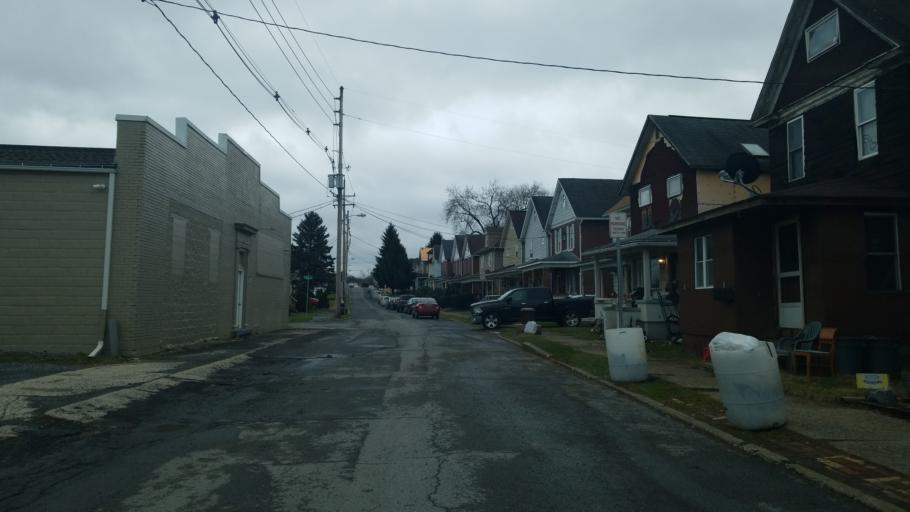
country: US
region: Pennsylvania
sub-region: Clearfield County
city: Sandy
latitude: 41.1157
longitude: -78.7698
